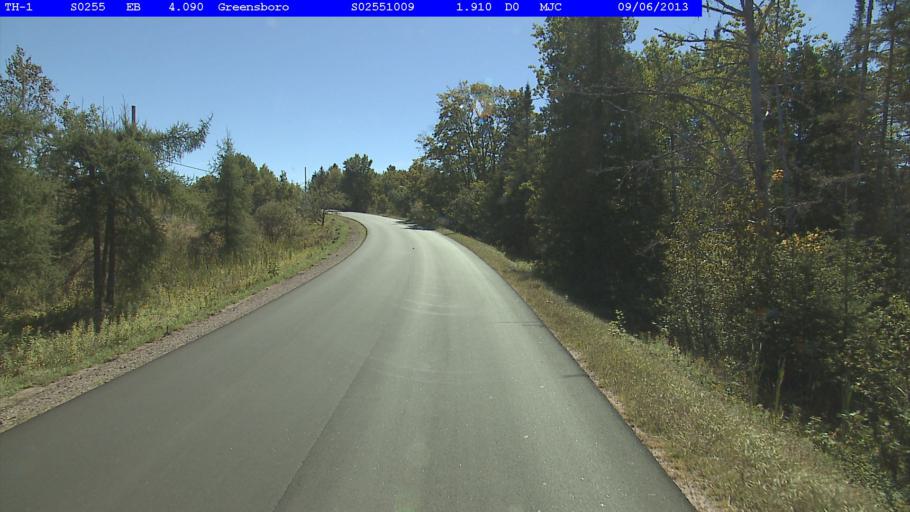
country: US
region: Vermont
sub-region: Caledonia County
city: Hardwick
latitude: 44.6142
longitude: -72.3245
